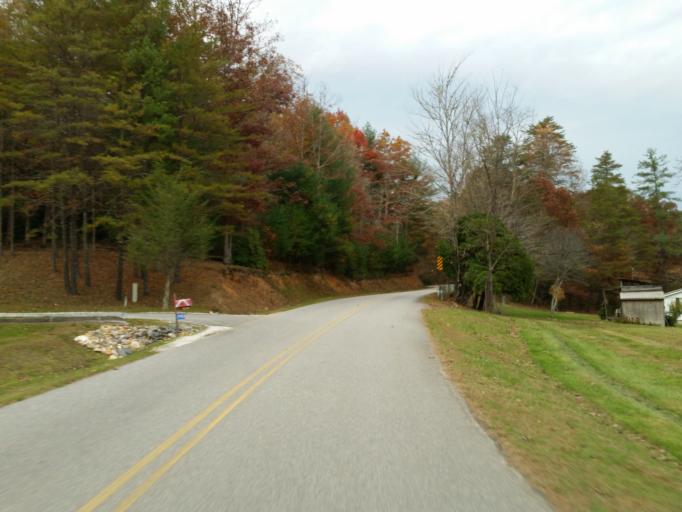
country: US
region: Georgia
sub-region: Fannin County
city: Blue Ridge
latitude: 34.7356
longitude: -84.1962
